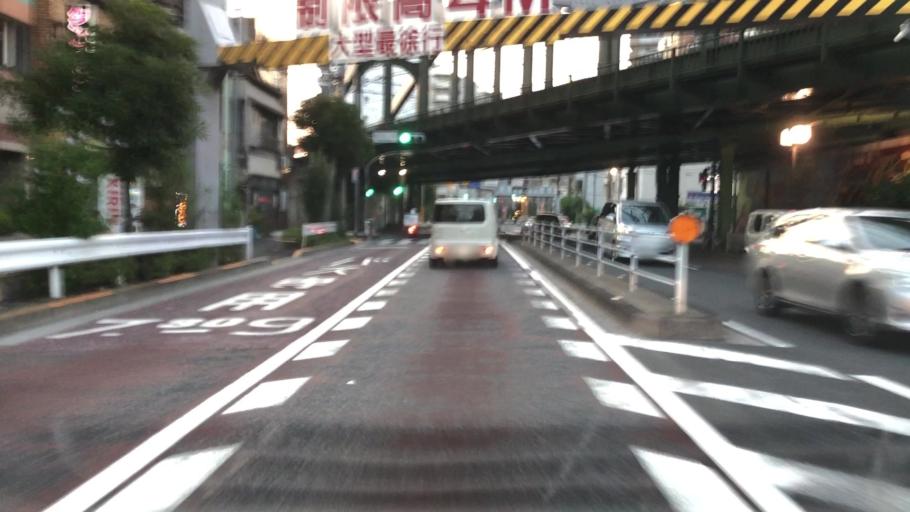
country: JP
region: Saitama
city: Soka
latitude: 35.7315
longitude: 139.7892
